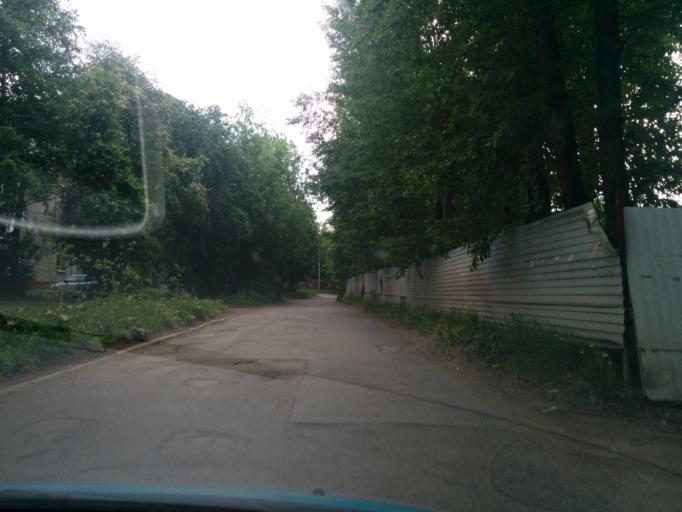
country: RU
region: Perm
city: Perm
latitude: 57.9945
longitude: 56.2040
